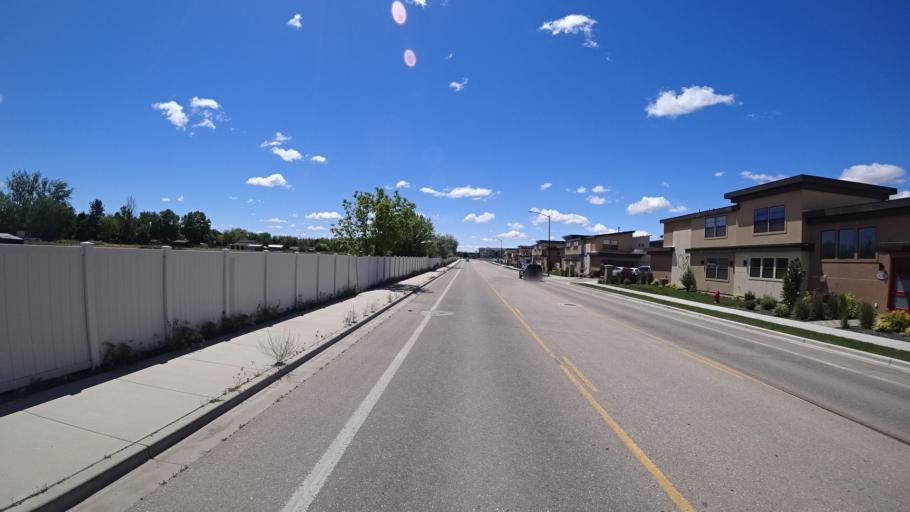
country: US
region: Idaho
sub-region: Ada County
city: Meridian
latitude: 43.6321
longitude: -116.3496
